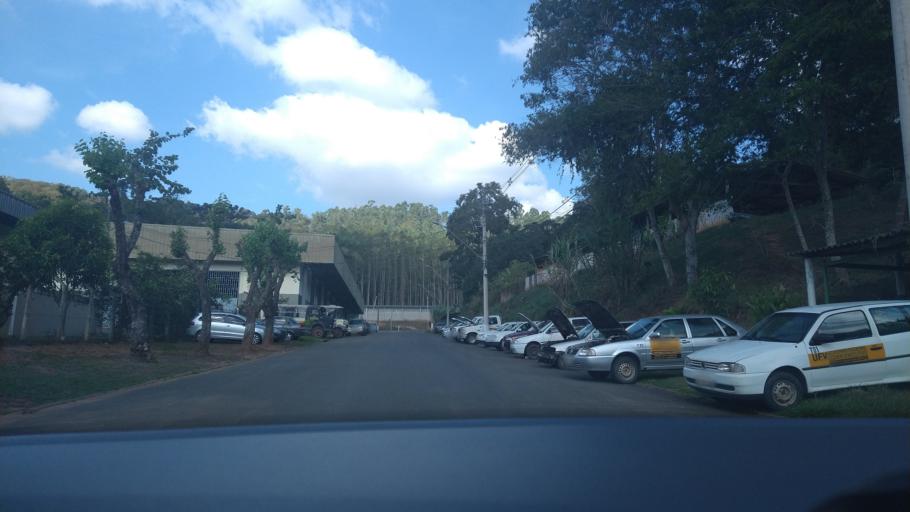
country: BR
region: Minas Gerais
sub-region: Vicosa
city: Vicosa
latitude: -20.7723
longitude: -42.8714
